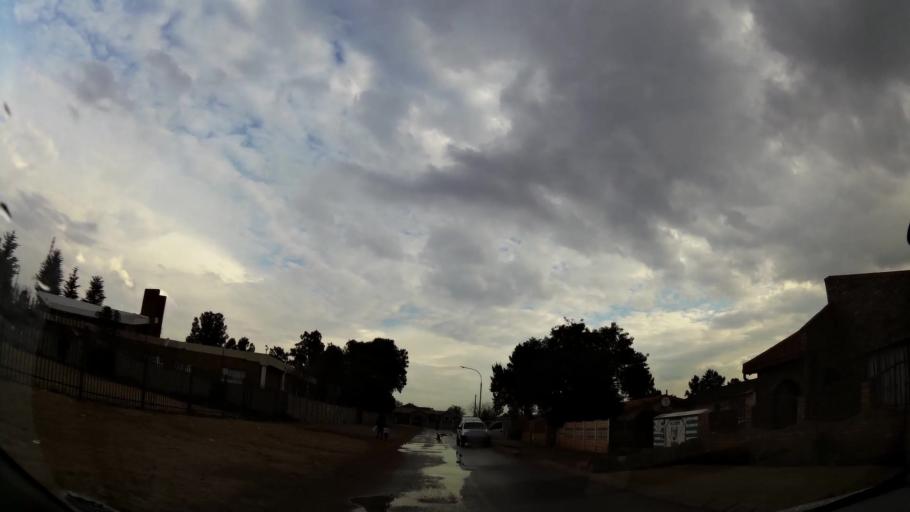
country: ZA
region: Gauteng
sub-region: Ekurhuleni Metropolitan Municipality
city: Germiston
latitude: -26.3737
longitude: 28.1255
